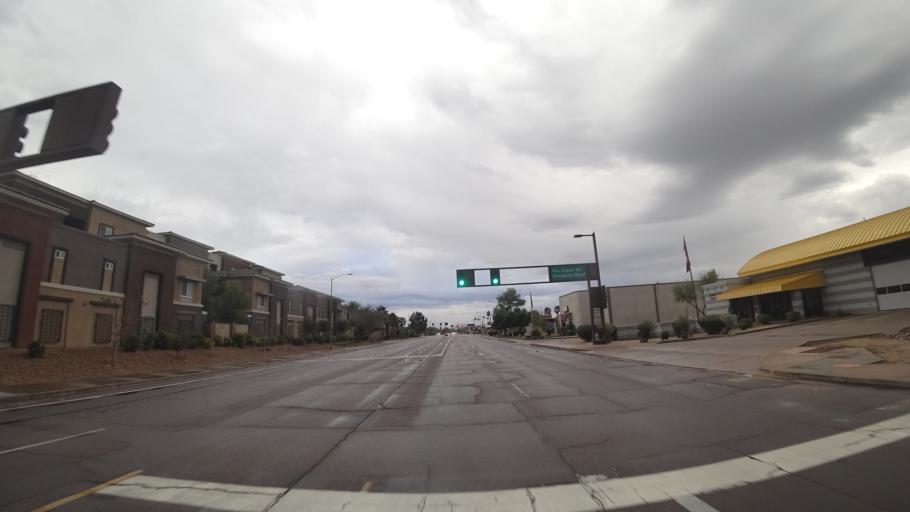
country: US
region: Arizona
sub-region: Maricopa County
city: Tempe Junction
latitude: 33.4402
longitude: -111.9286
